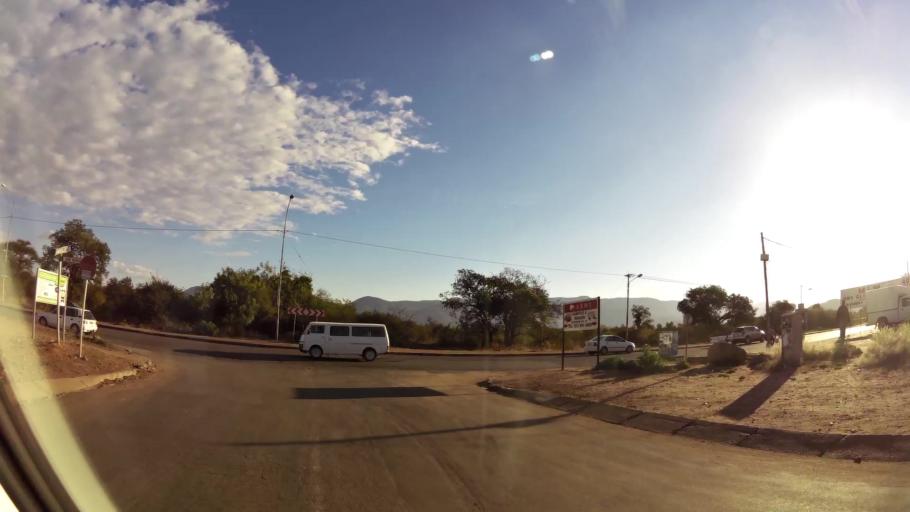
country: ZA
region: Limpopo
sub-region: Waterberg District Municipality
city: Mokopane
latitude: -24.1731
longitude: 29.0008
